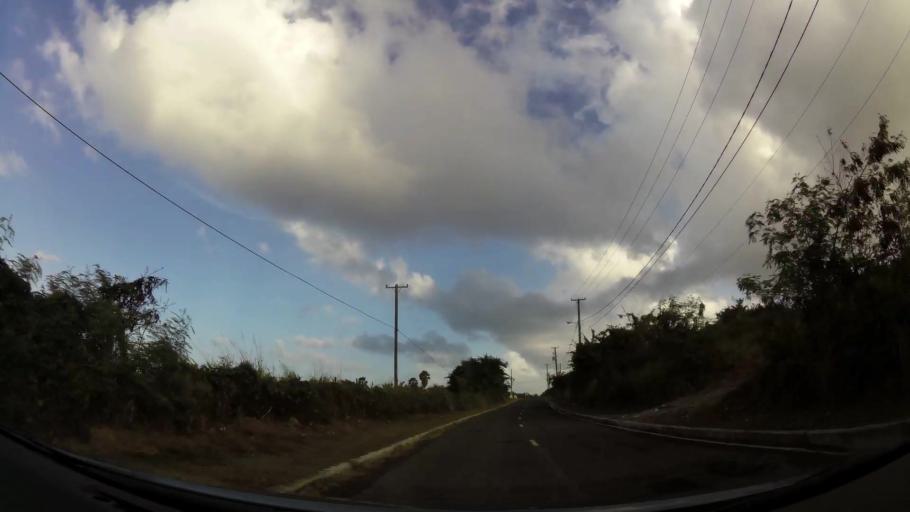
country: KN
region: Saint James Windwa
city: Newcastle
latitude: 17.1912
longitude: -62.5642
